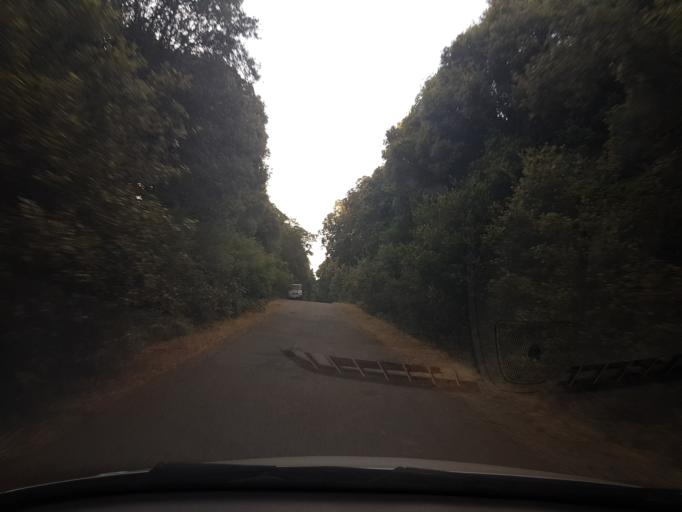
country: IT
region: Sardinia
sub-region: Provincia di Oristano
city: Seneghe
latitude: 40.1086
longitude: 8.5875
